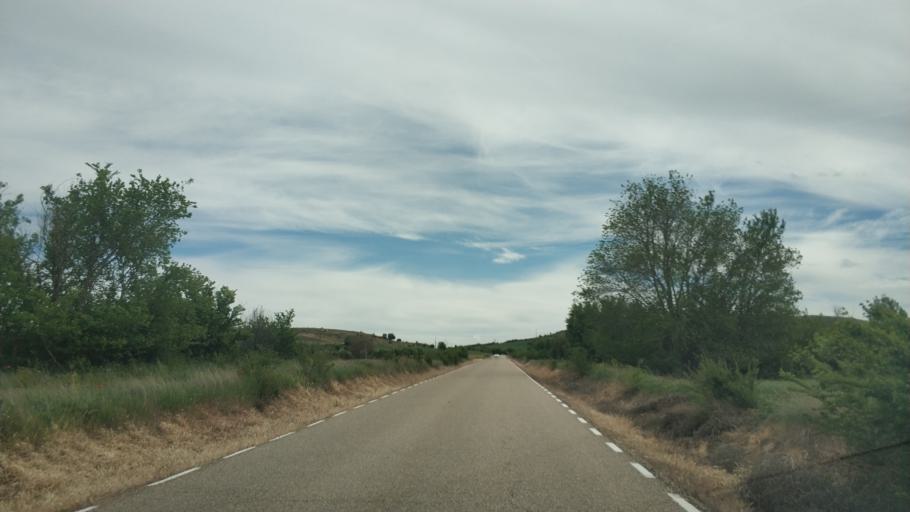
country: ES
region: Castille and Leon
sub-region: Provincia de Soria
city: Berlanga de Duero
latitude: 41.4862
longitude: -2.8661
